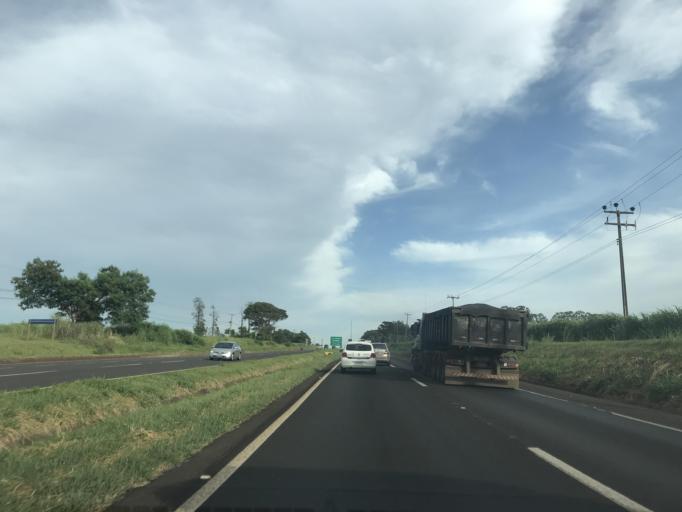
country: BR
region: Parana
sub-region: Maringa
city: Maringa
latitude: -23.4027
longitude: -51.9971
